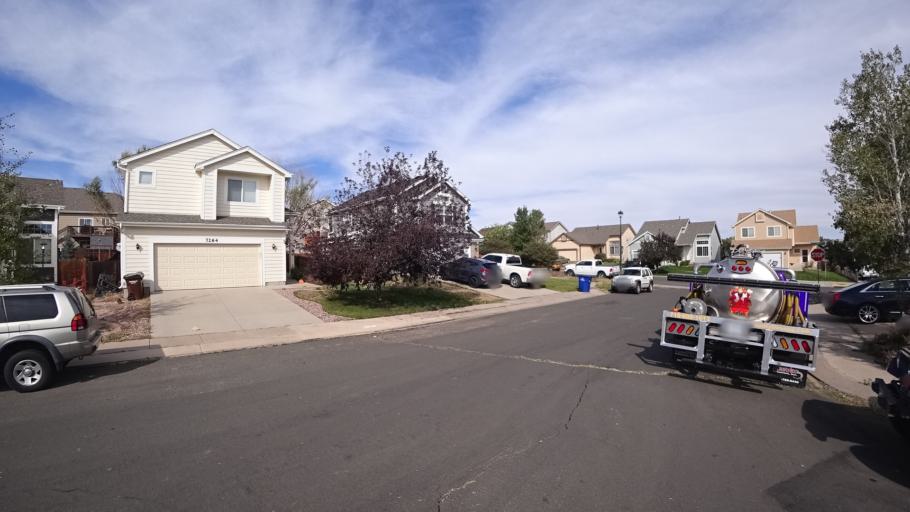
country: US
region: Colorado
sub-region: El Paso County
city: Cimarron Hills
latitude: 38.9096
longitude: -104.6934
